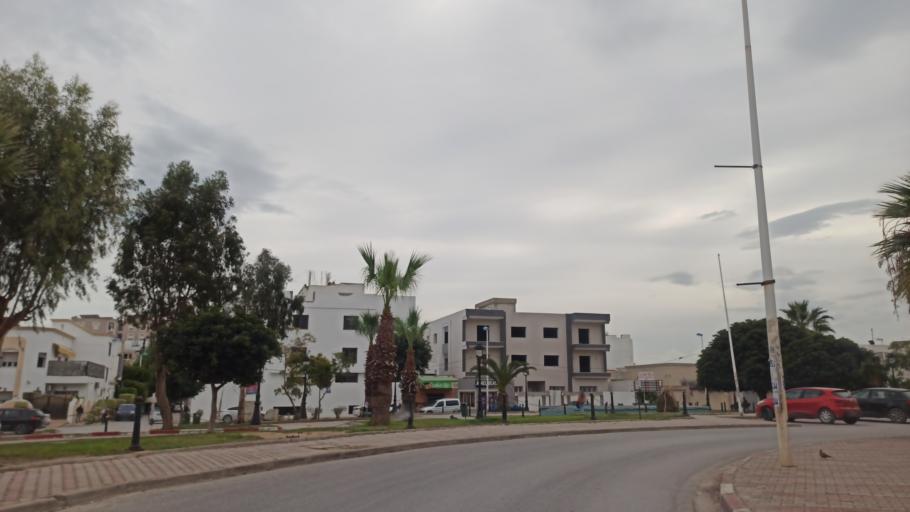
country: TN
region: Tunis
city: La Goulette
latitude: 36.8586
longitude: 10.2655
